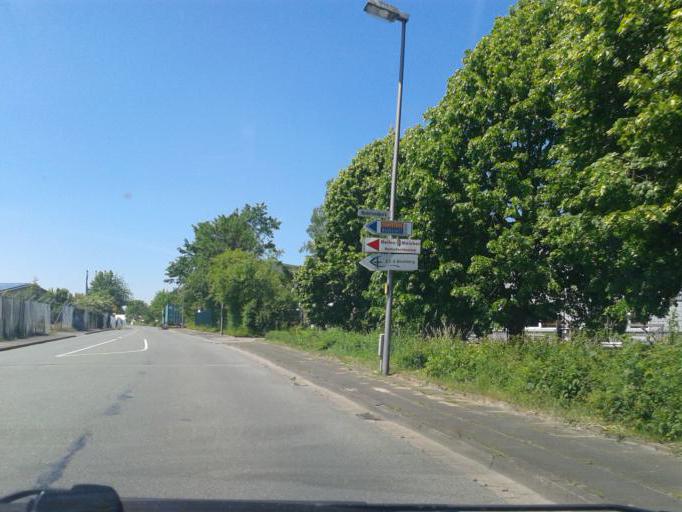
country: DE
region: North Rhine-Westphalia
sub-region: Regierungsbezirk Detmold
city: Blomberg
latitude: 51.9320
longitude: 9.0952
